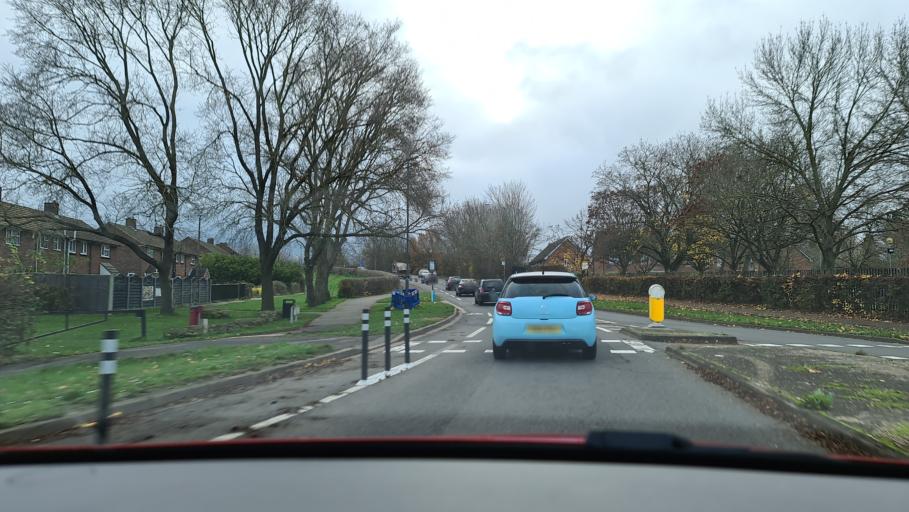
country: GB
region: England
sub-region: Buckinghamshire
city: Aylesbury
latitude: 51.8003
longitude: -0.8131
